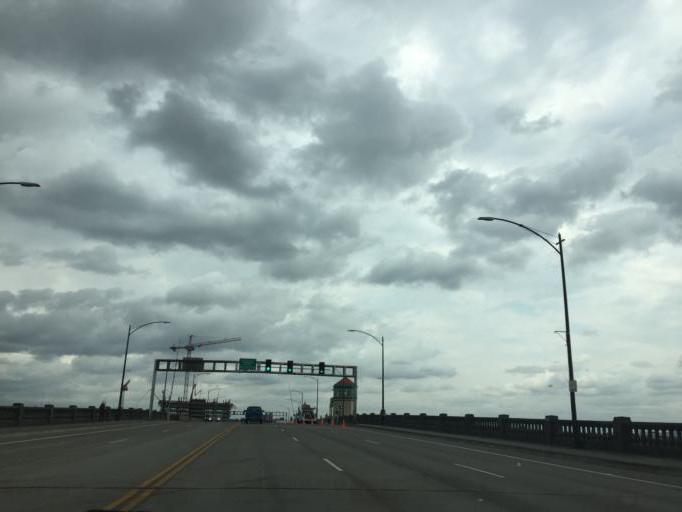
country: US
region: Oregon
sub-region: Multnomah County
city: Portland
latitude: 45.5231
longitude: -122.6697
